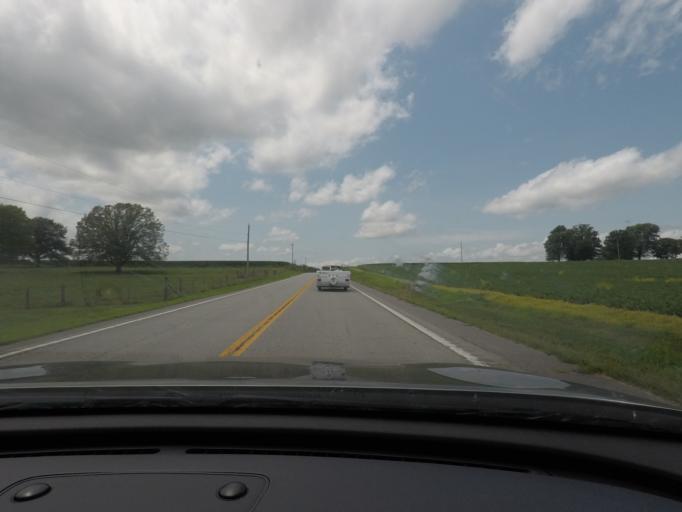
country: US
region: Missouri
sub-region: Carroll County
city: Carrollton
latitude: 39.2025
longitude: -93.4570
